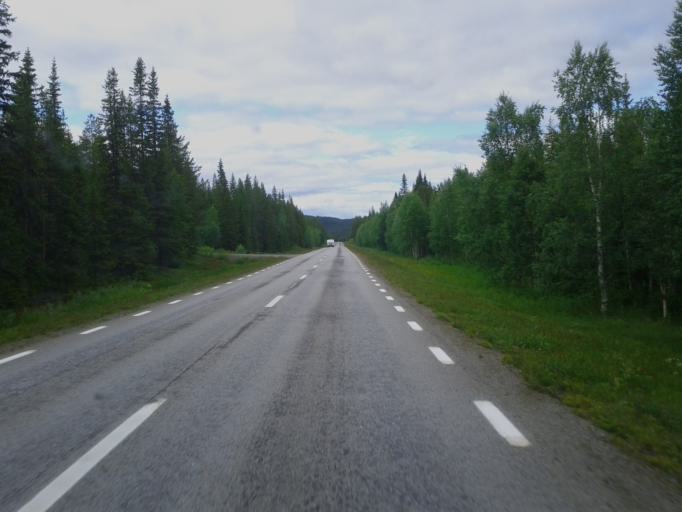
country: SE
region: Vaesterbotten
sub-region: Storumans Kommun
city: Fristad
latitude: 65.3563
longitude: 16.5592
